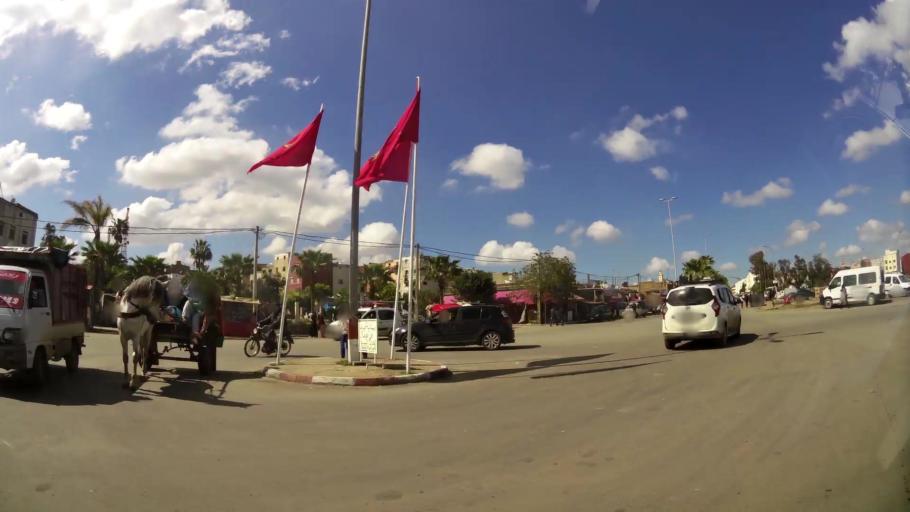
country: MA
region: Grand Casablanca
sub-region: Mediouna
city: Mediouna
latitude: 33.4539
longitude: -7.5186
